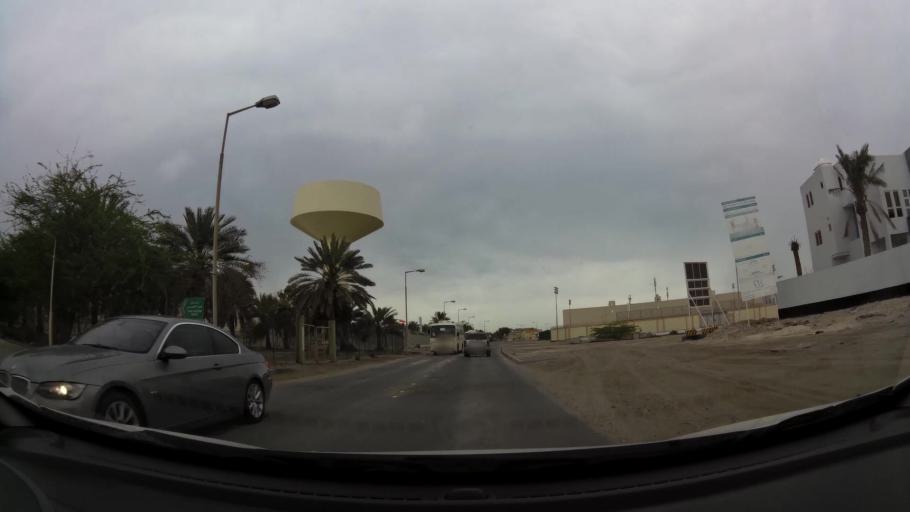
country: BH
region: Central Governorate
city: Madinat Hamad
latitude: 26.1402
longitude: 50.4600
